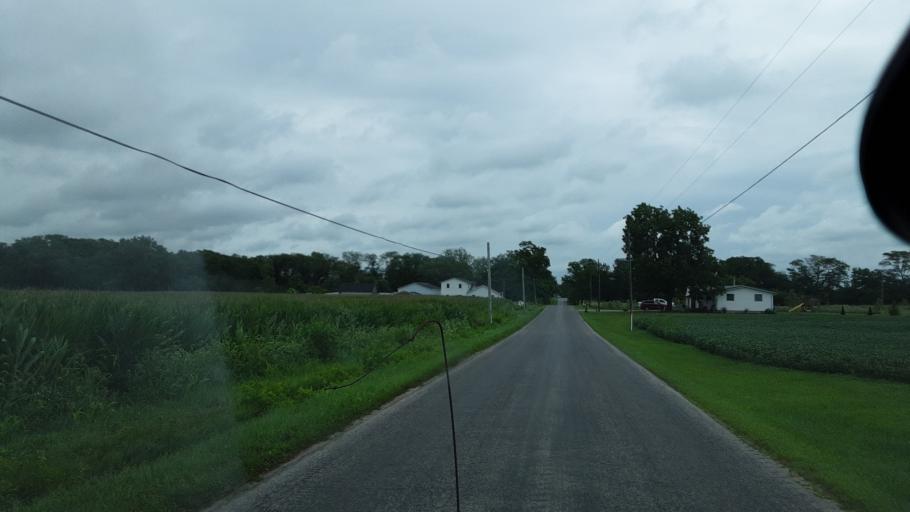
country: US
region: Indiana
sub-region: Adams County
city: Geneva
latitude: 40.5331
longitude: -84.9977
